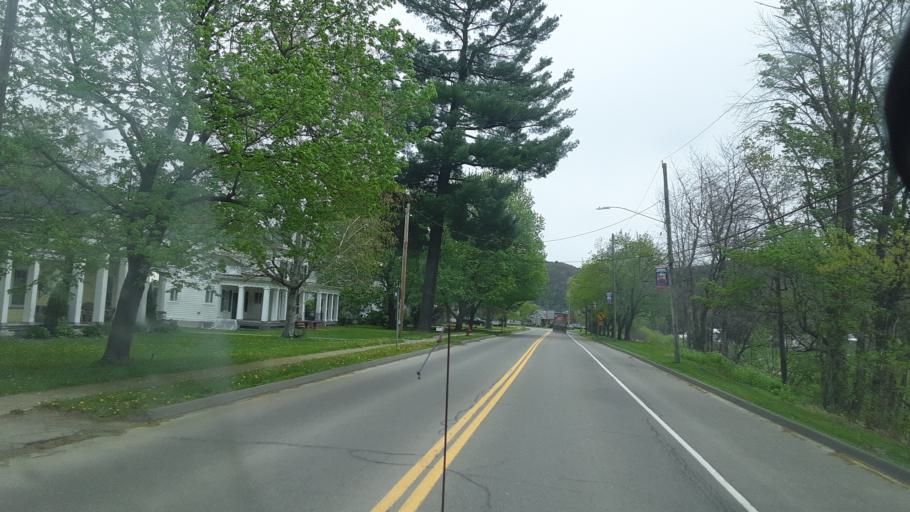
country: US
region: New York
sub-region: Steuben County
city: Addison
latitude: 42.1030
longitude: -77.2398
